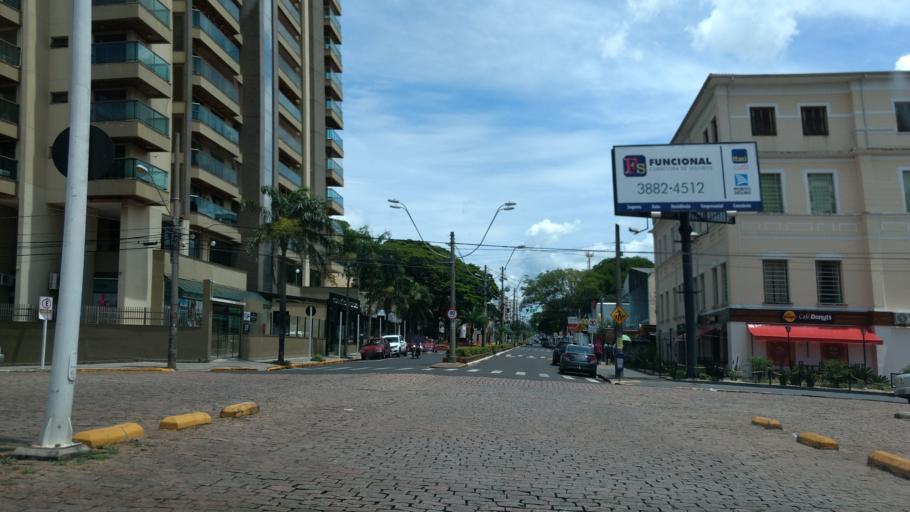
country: BR
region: Sao Paulo
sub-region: Botucatu
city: Botucatu
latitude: -22.8862
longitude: -48.4446
